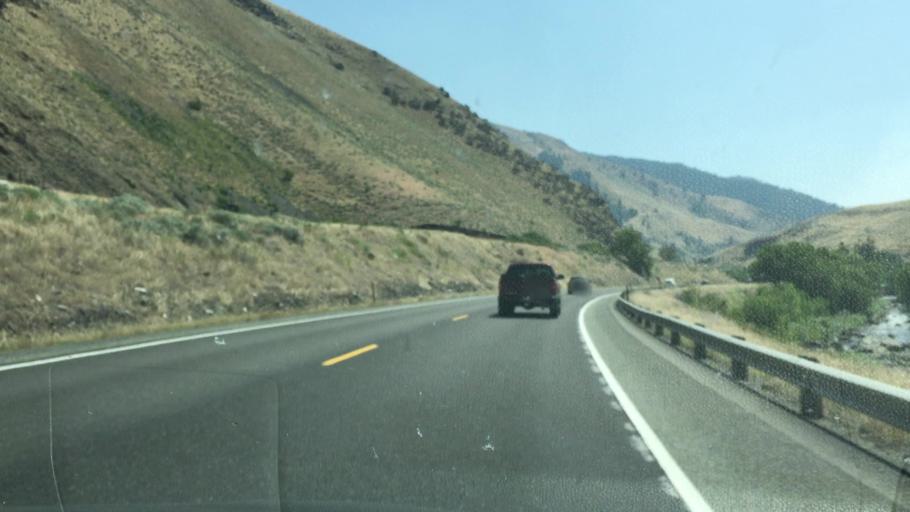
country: US
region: Idaho
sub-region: Valley County
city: McCall
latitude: 45.3529
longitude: -116.3570
